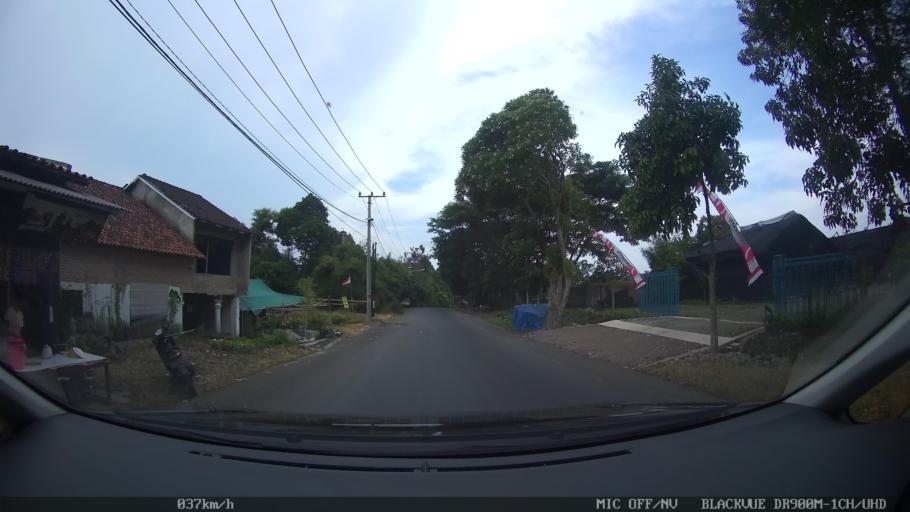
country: ID
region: Lampung
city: Bandarlampung
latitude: -5.4211
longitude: 105.1880
